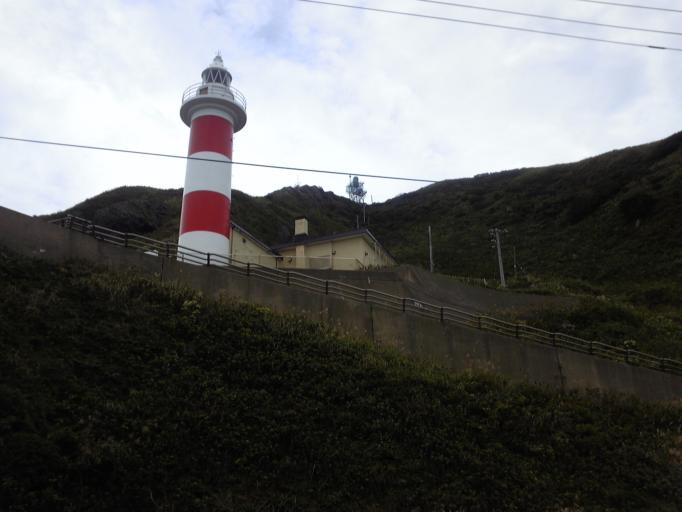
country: JP
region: Aomori
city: Shimokizukuri
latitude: 41.3978
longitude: 140.1974
